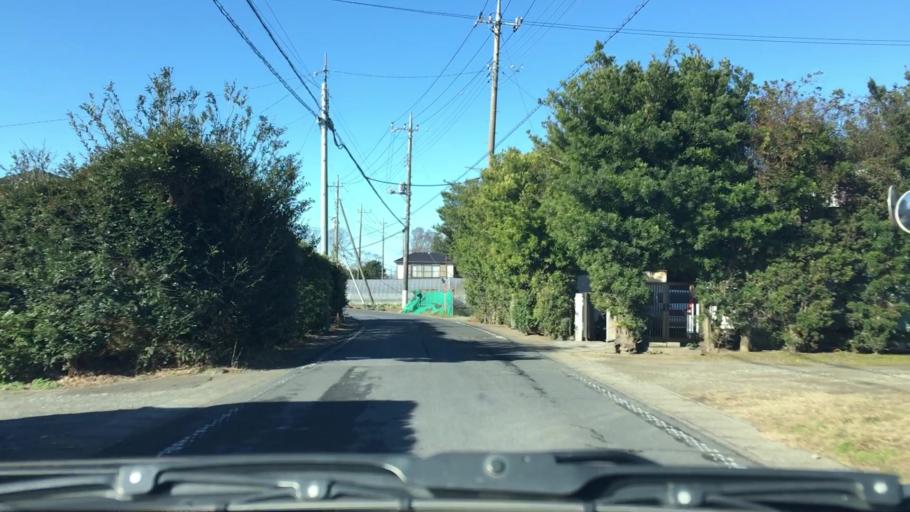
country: JP
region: Chiba
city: Omigawa
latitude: 35.8659
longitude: 140.6586
